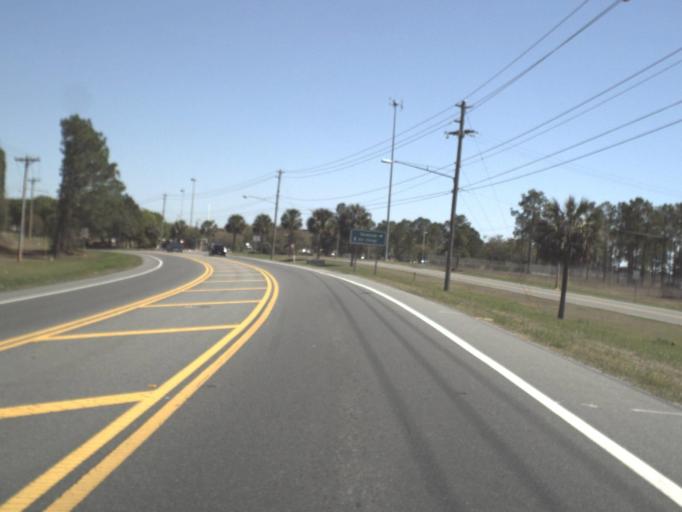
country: US
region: Florida
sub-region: Leon County
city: Tallahassee
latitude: 30.3984
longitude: -84.3510
